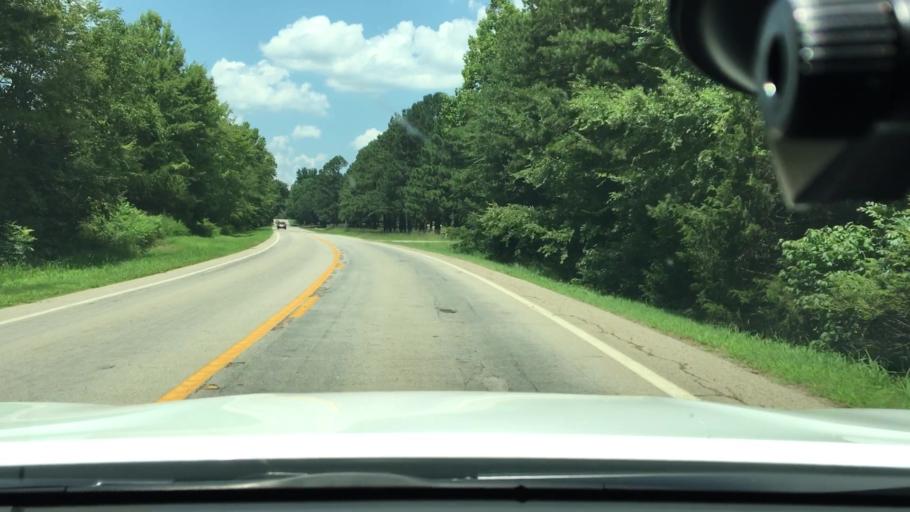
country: US
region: Arkansas
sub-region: Logan County
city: Booneville
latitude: 35.2102
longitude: -93.9265
